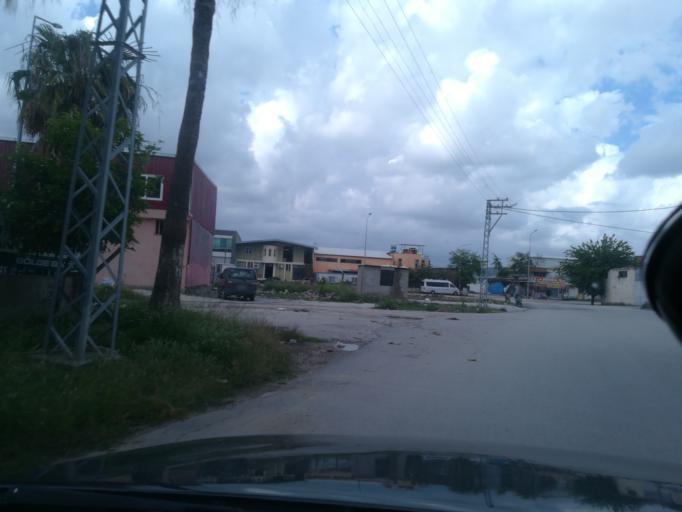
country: TR
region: Adana
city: Yuregir
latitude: 36.9768
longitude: 35.3912
